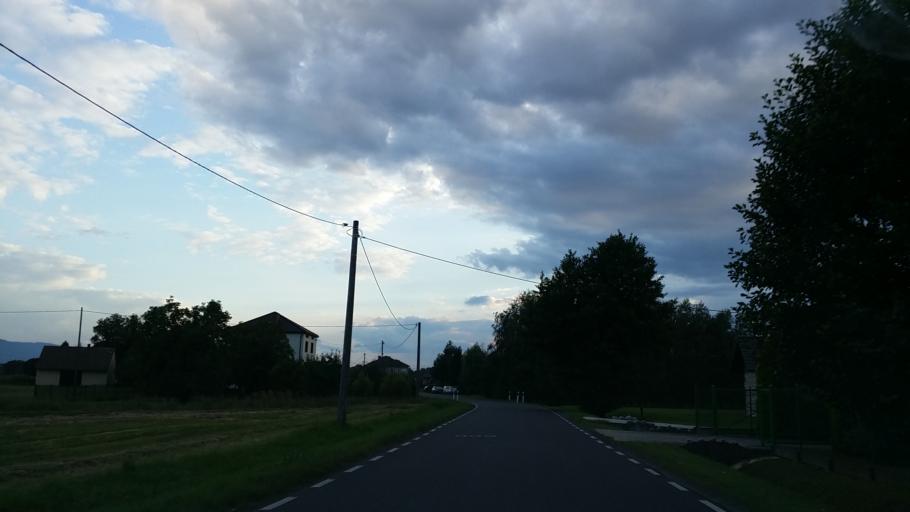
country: PL
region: Lesser Poland Voivodeship
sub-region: Powiat oswiecimski
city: Malec
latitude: 49.9144
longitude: 19.2342
